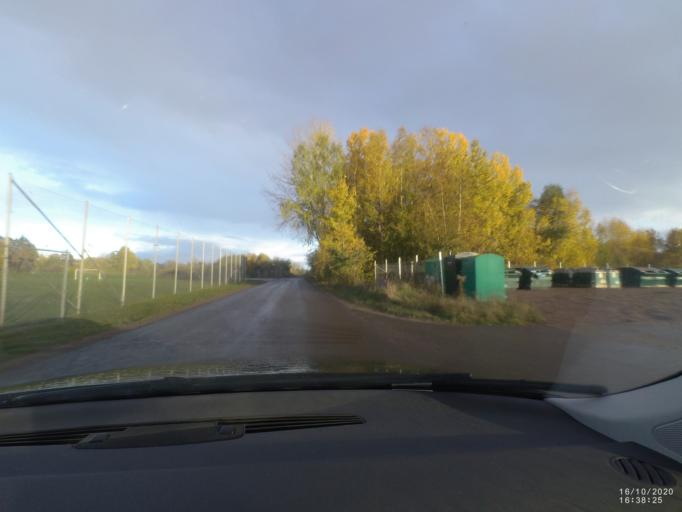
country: SE
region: Soedermanland
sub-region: Nykopings Kommun
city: Nykoping
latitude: 58.7479
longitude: 17.0471
